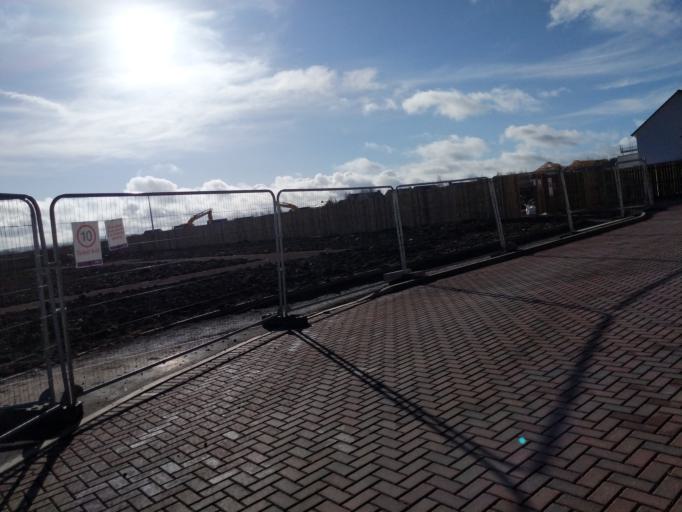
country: GB
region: Scotland
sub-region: Midlothian
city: Loanhead
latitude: 55.8518
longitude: -3.1432
